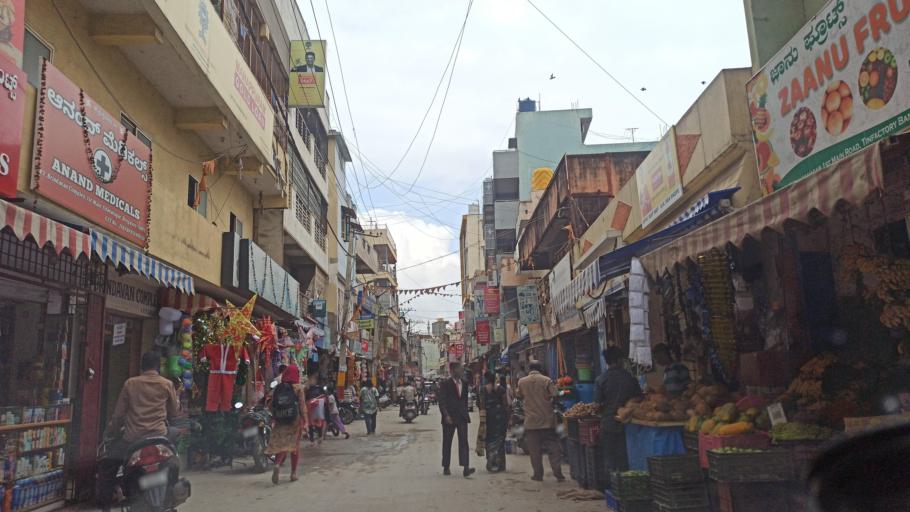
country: IN
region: Karnataka
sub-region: Bangalore Urban
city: Bangalore
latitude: 12.9957
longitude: 77.6723
